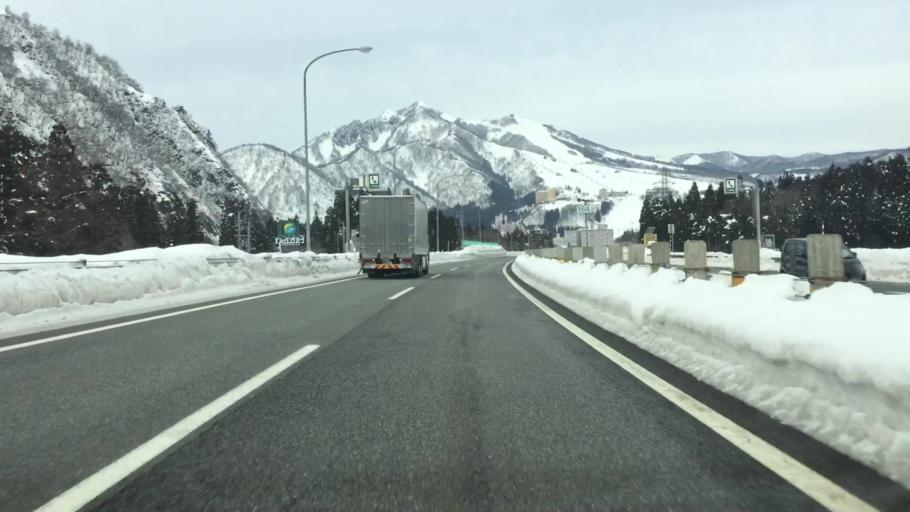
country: JP
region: Niigata
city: Shiozawa
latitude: 36.9129
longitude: 138.8395
